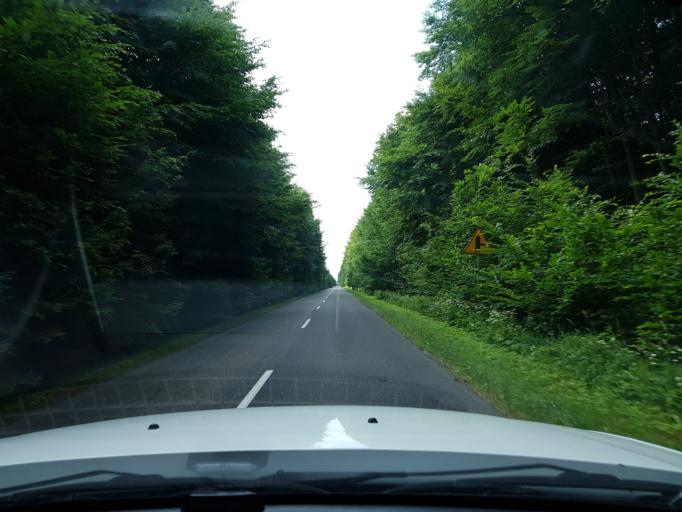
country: PL
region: West Pomeranian Voivodeship
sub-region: Powiat gryfinski
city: Banie
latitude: 53.0112
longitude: 14.7220
